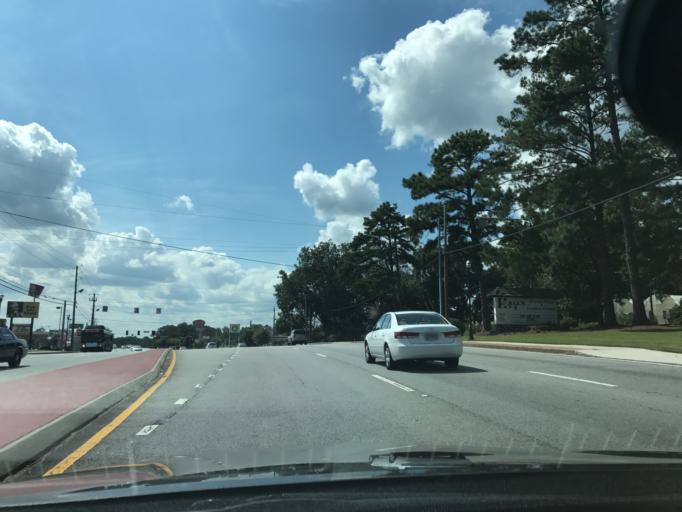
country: US
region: Georgia
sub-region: DeKalb County
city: Stone Mountain
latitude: 33.8010
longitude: -84.2037
